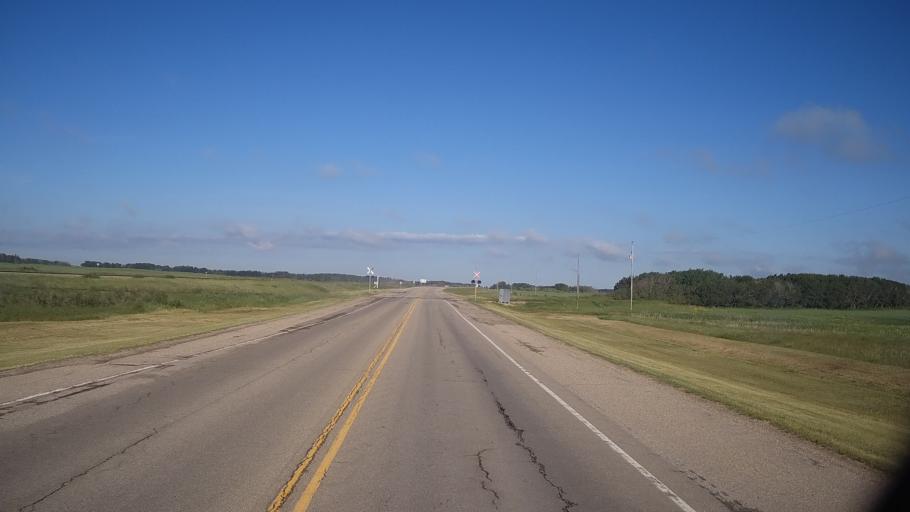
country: CA
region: Saskatchewan
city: Lanigan
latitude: 51.8495
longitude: -105.0546
